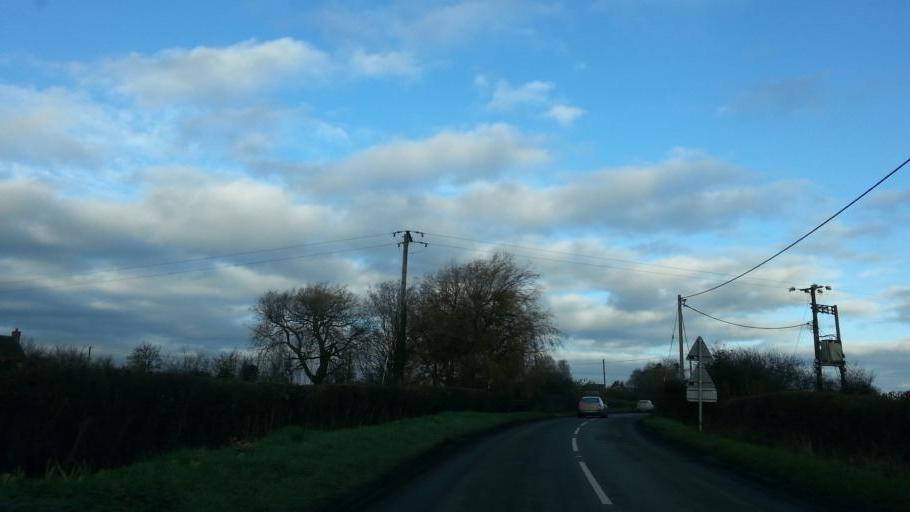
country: GB
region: England
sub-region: Oxfordshire
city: Shrivenham
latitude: 51.6119
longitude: -1.6104
